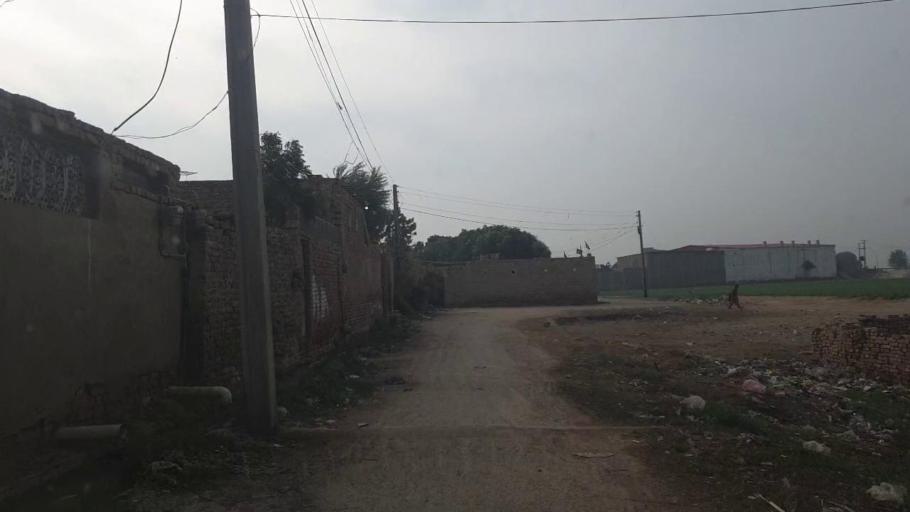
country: PK
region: Sindh
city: Tando Adam
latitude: 25.7478
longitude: 68.6606
